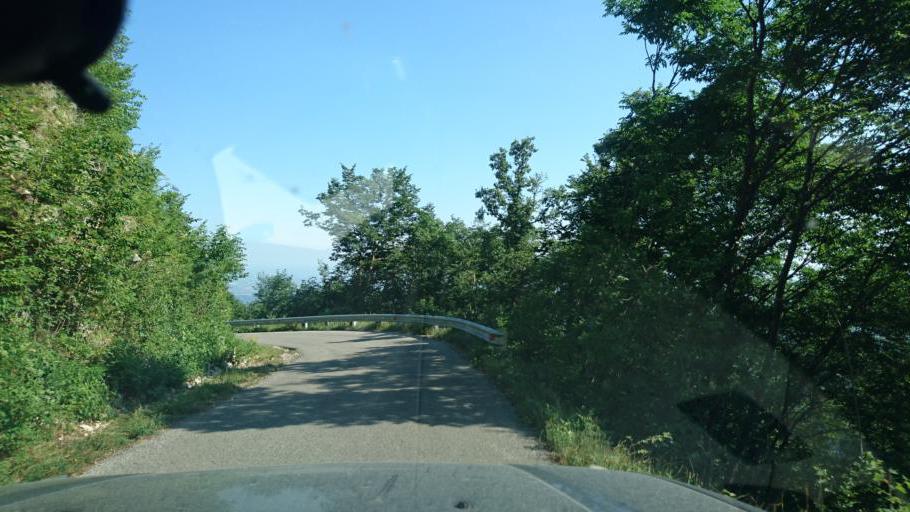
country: IT
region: Veneto
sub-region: Provincia di Treviso
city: Crespano del Grappa
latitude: 45.8640
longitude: 11.8429
